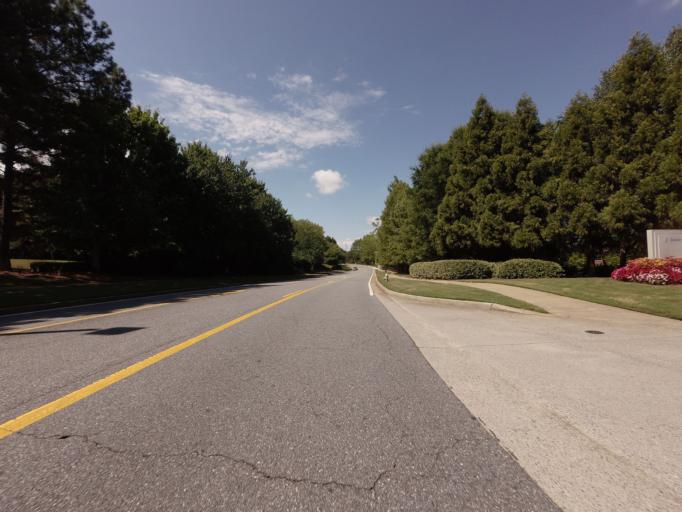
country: US
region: Georgia
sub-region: Fulton County
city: Johns Creek
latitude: 34.0580
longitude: -84.1706
